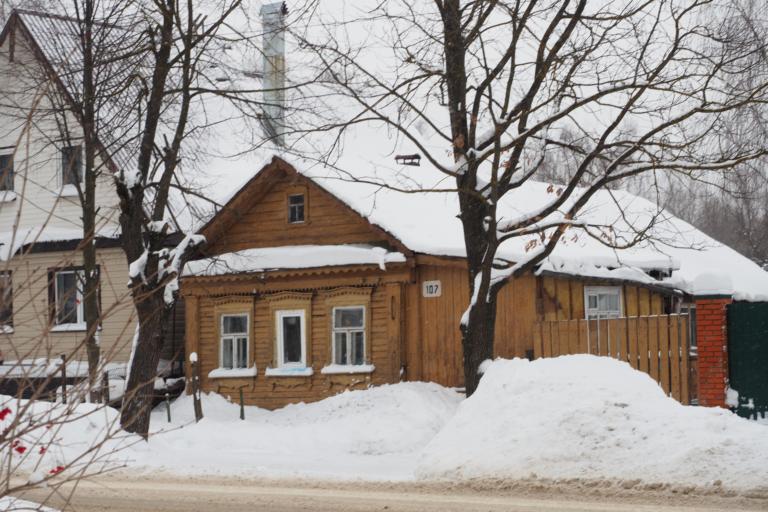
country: RU
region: Moskovskaya
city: Yegor'yevsk
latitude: 55.3794
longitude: 39.0194
